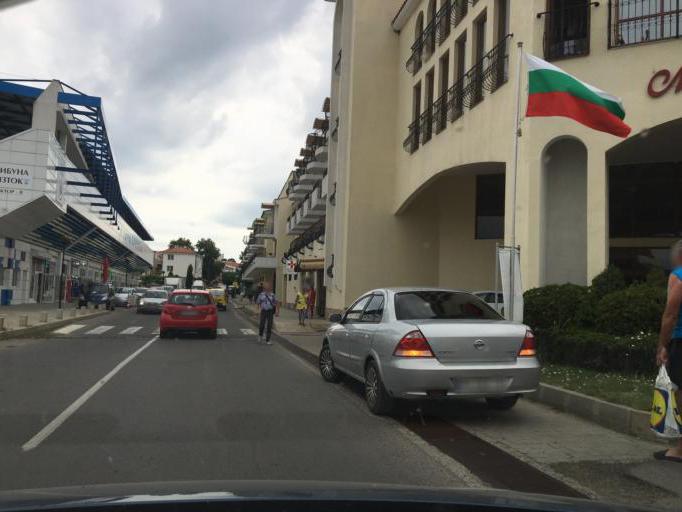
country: BG
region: Burgas
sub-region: Obshtina Sozopol
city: Sozopol
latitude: 42.4131
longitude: 27.6979
